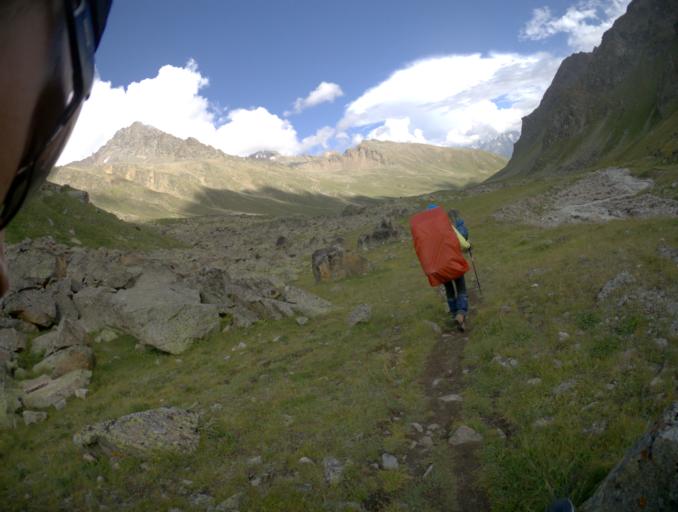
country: RU
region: Kabardino-Balkariya
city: Terskol
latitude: 43.3236
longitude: 42.5708
